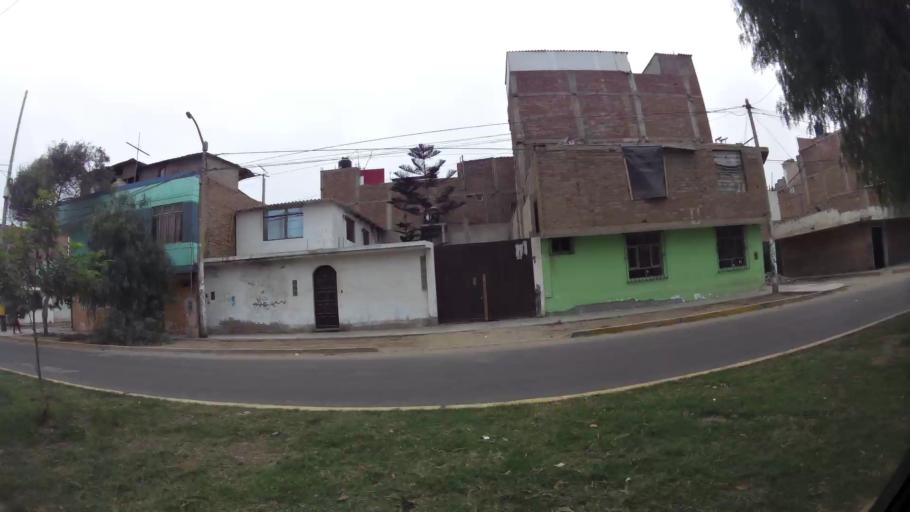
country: PE
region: La Libertad
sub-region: Provincia de Trujillo
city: Buenos Aires
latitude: -8.1393
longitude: -79.0457
